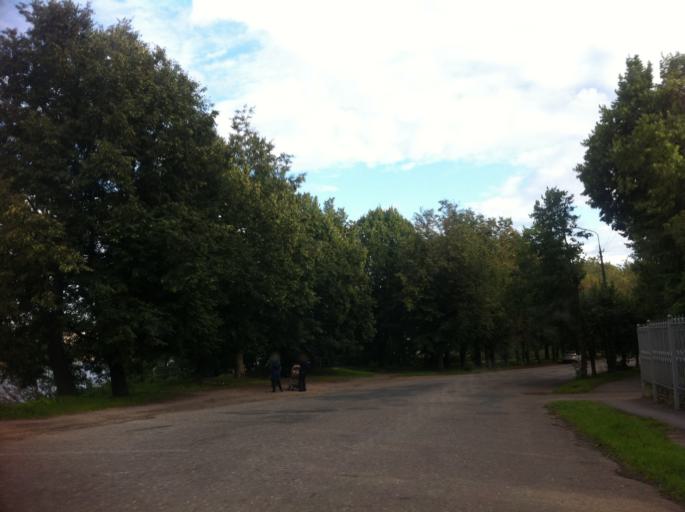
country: RU
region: Pskov
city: Pskov
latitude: 57.8258
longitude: 28.3186
